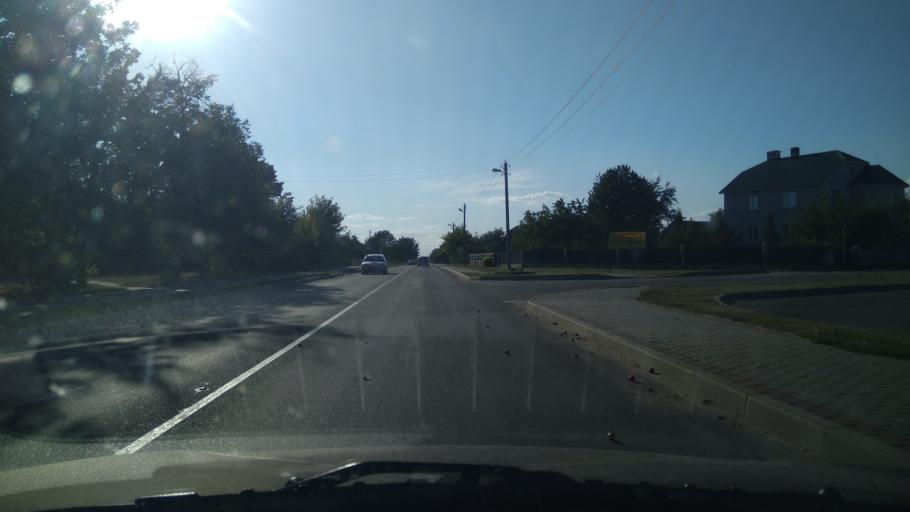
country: BY
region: Brest
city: Byaroza
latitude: 52.5413
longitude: 24.9754
